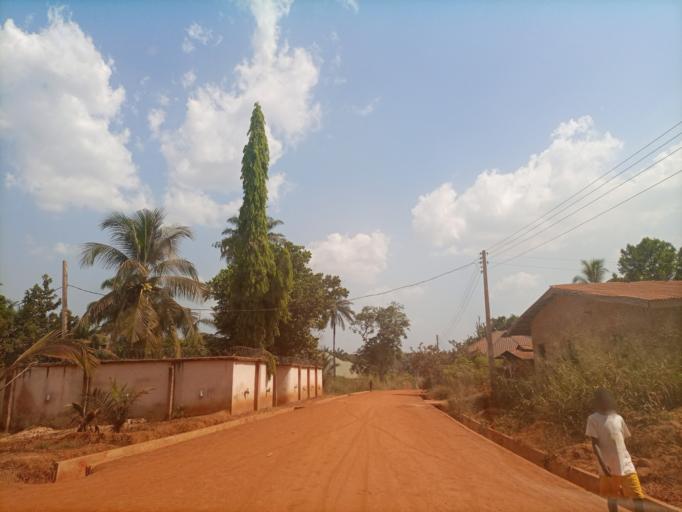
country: NG
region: Enugu
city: Obolo-Eke (1)
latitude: 6.8649
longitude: 7.6587
